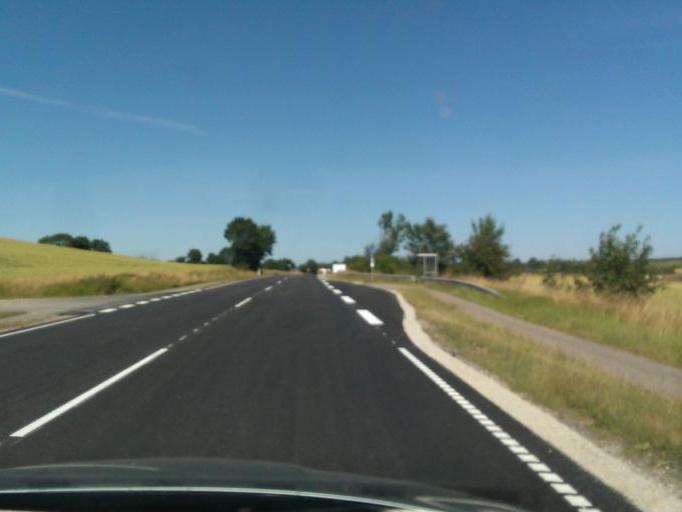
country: DK
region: Central Jutland
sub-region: Arhus Kommune
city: Malling
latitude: 56.0233
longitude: 10.1809
